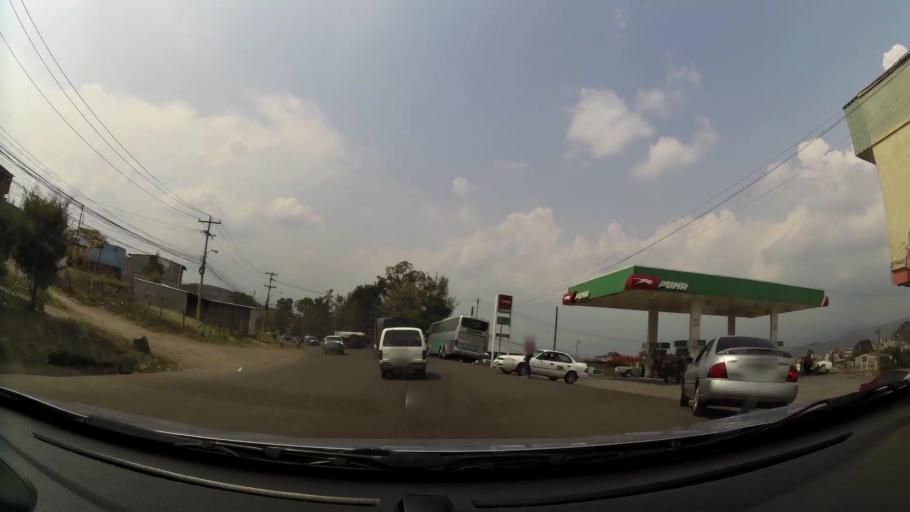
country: HN
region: Francisco Morazan
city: El Lolo
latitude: 14.1238
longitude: -87.2244
